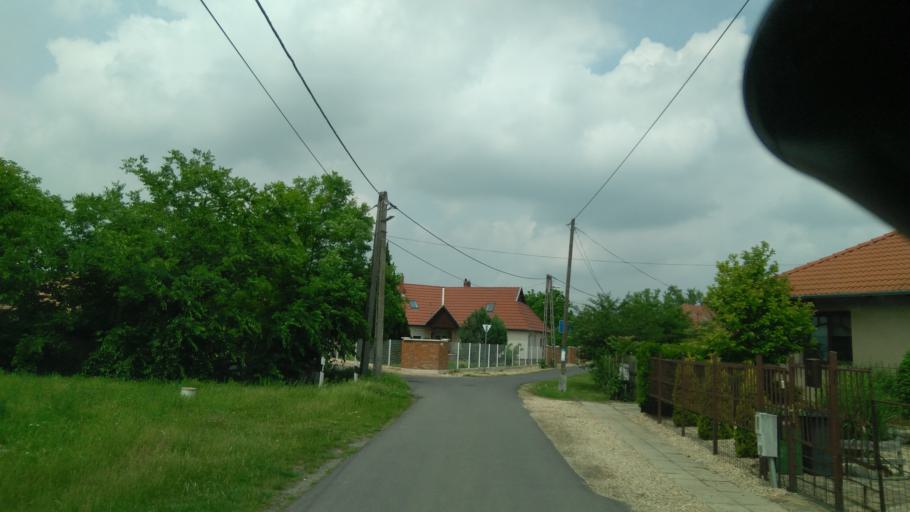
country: HU
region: Bekes
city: Gyula
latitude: 46.6597
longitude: 21.2570
